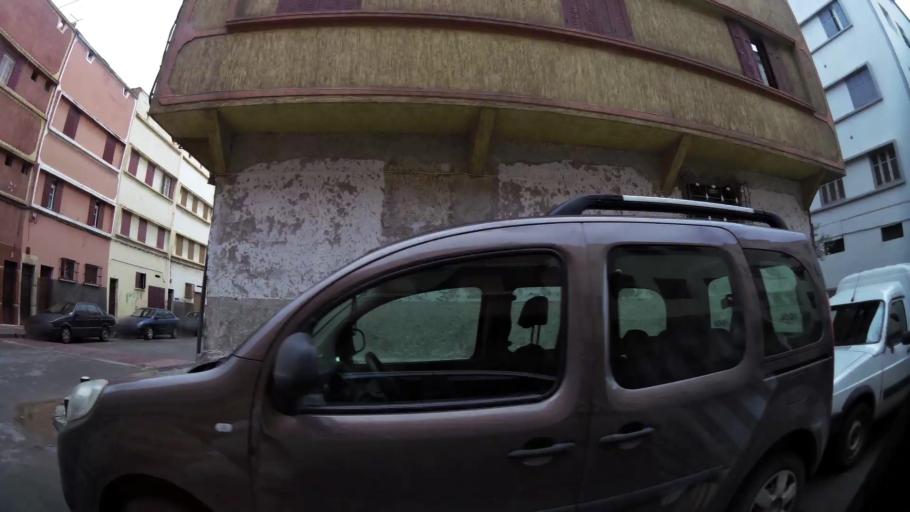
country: MA
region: Grand Casablanca
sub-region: Casablanca
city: Casablanca
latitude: 33.5395
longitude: -7.5749
